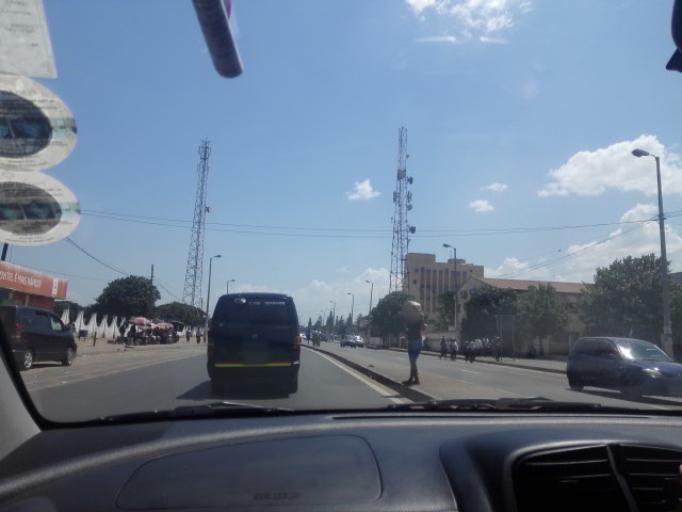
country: MZ
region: Maputo City
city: Maputo
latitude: -25.9353
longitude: 32.5498
